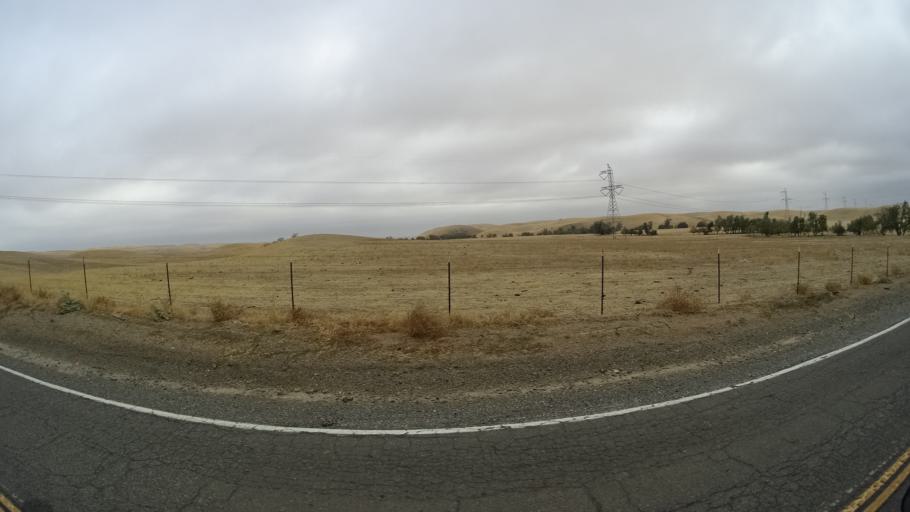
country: US
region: California
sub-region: Yolo County
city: Dunnigan
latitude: 38.8431
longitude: -122.0440
